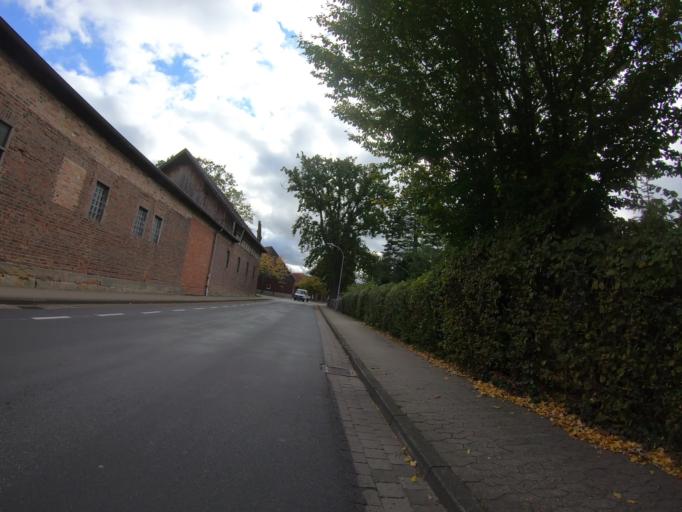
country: DE
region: Lower Saxony
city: Wasbuttel
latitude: 52.4117
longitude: 10.5922
